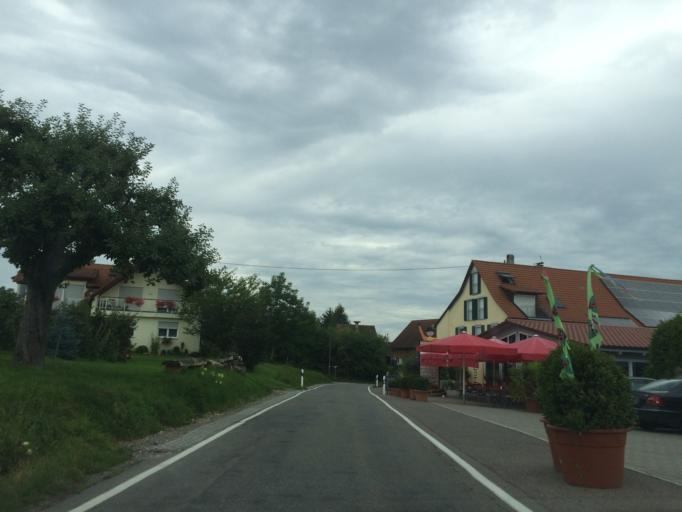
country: DE
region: Baden-Wuerttemberg
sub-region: Tuebingen Region
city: Immenstaad am Bodensee
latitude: 47.6846
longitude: 9.3484
